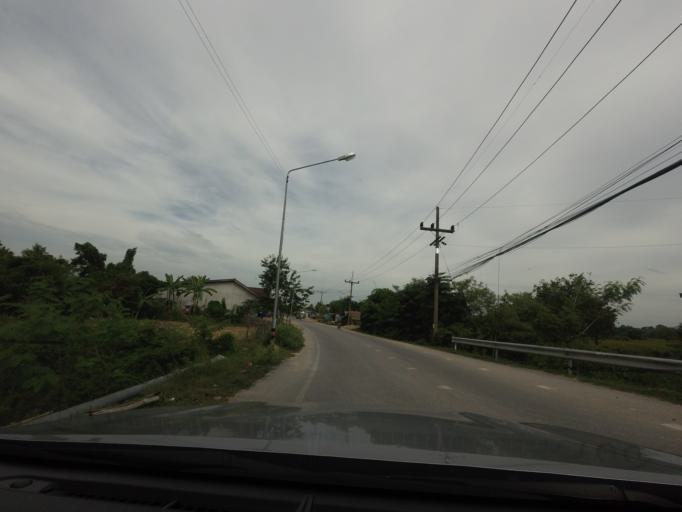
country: TH
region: Yala
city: Raman
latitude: 6.4545
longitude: 101.4464
